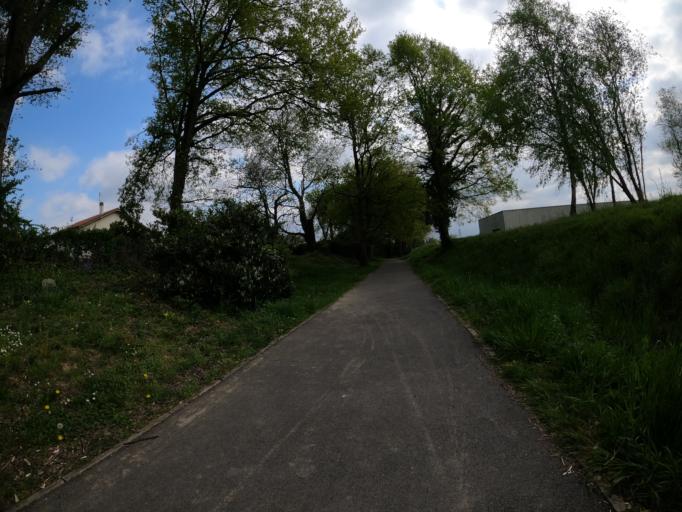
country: FR
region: Aquitaine
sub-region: Departement des Pyrenees-Atlantiques
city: Lons
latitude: 43.3311
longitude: -0.3824
